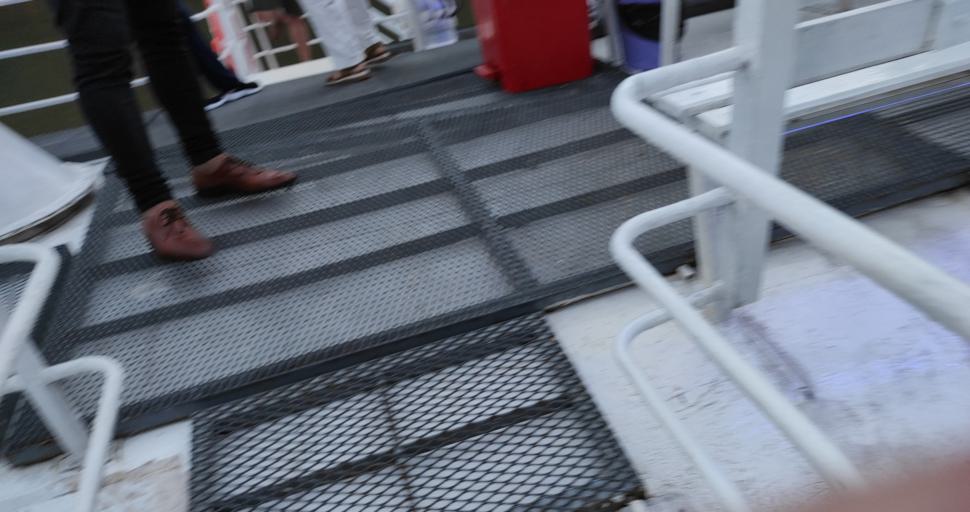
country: AR
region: Misiones
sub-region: Departamento de Iguazu
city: Puerto Iguazu
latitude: -25.5910
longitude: -54.5759
